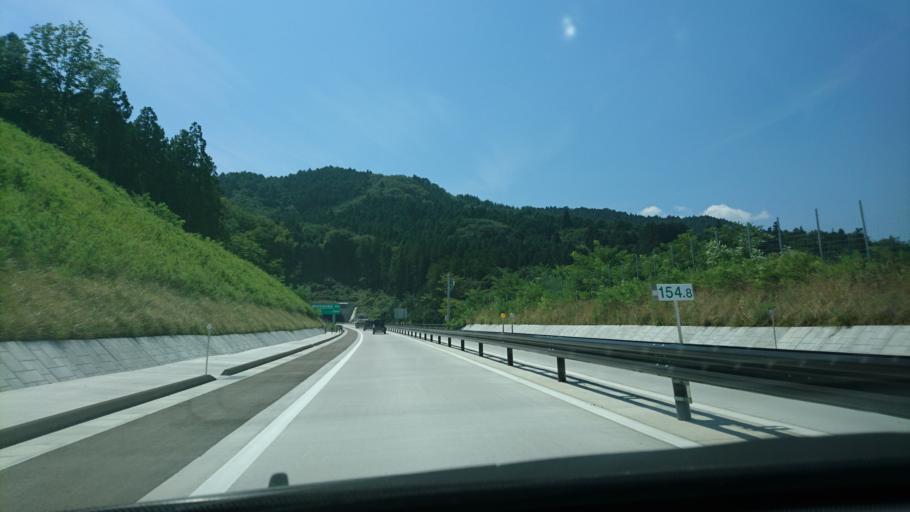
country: JP
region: Iwate
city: Ofunato
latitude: 39.0255
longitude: 141.6136
